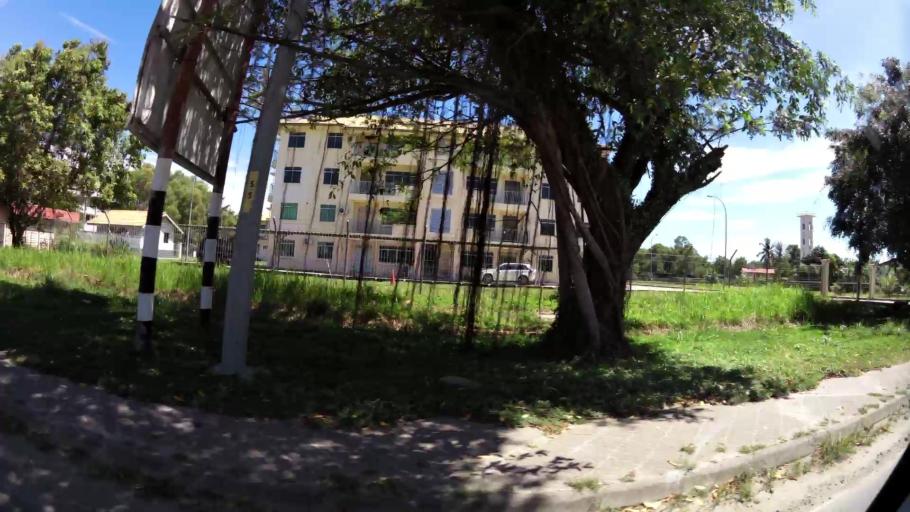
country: BN
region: Brunei and Muara
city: Bandar Seri Begawan
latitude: 5.0279
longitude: 115.0665
